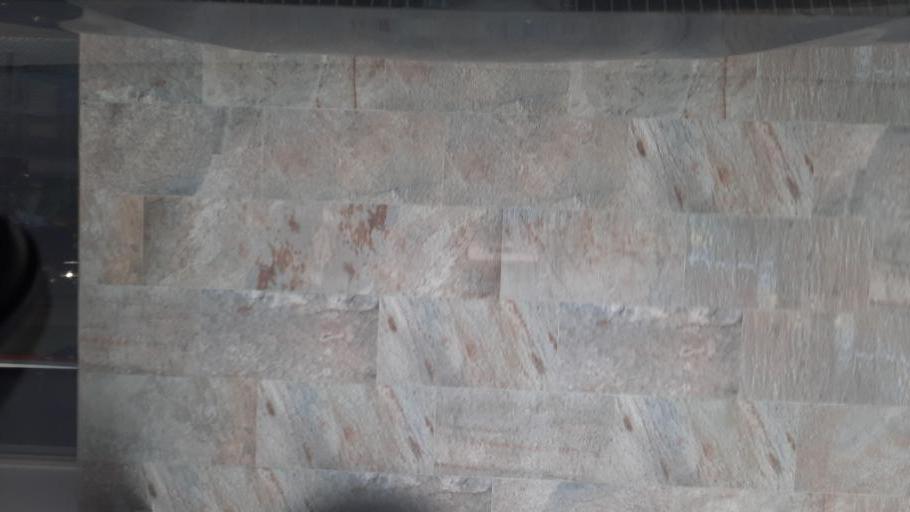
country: HN
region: Choluteca
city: Ciudad Choluteca
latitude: 13.3238
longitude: -87.2143
